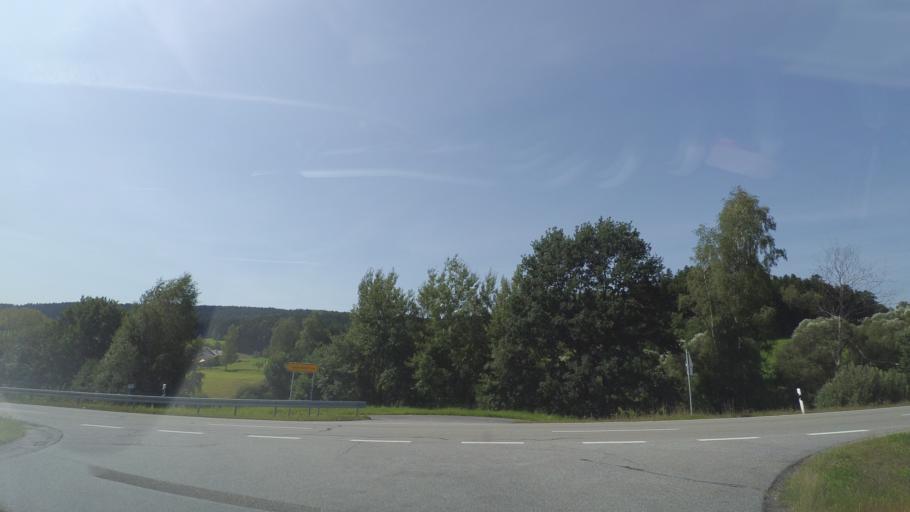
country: DE
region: Bavaria
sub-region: Lower Bavaria
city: Geiersthal
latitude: 49.0525
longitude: 12.9725
